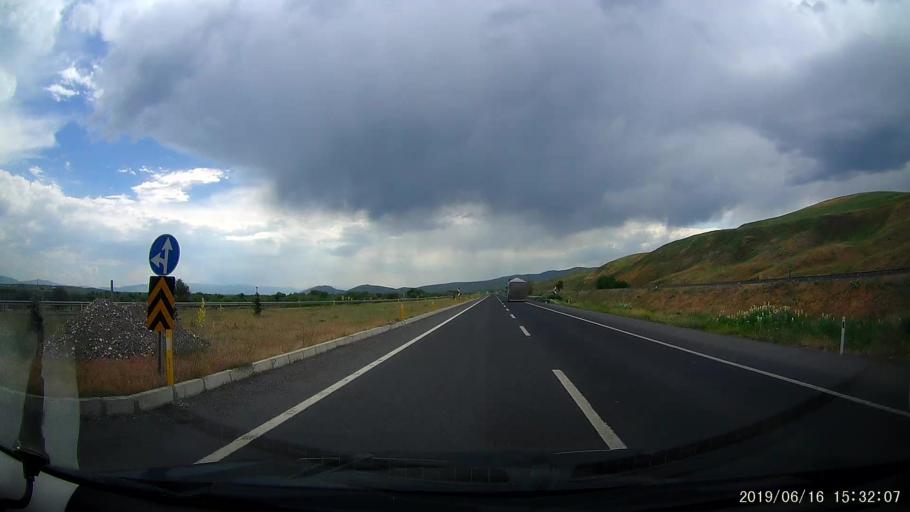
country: TR
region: Erzurum
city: Horasan
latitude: 40.0302
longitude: 42.0574
